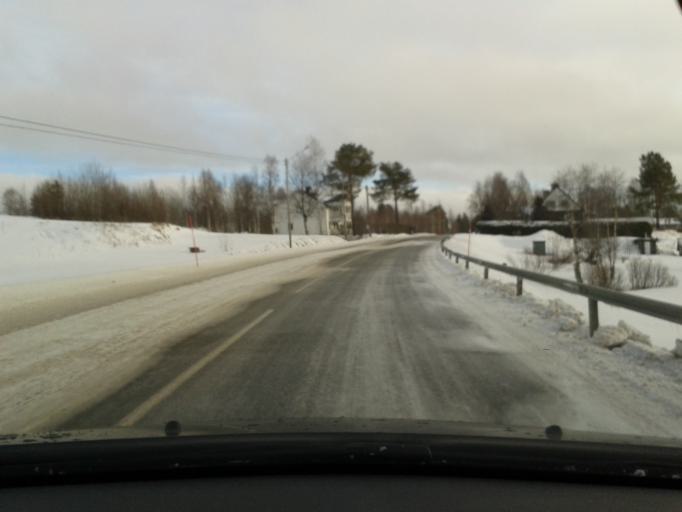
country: SE
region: Vaesterbotten
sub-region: Vilhelmina Kommun
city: Sjoberg
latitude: 64.6327
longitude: 16.3989
